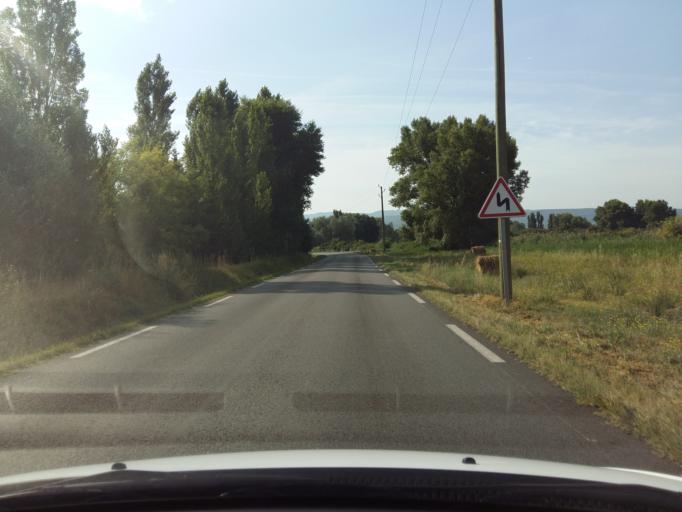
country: FR
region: Provence-Alpes-Cote d'Azur
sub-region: Departement du Vaucluse
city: Gargas
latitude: 43.9008
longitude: 5.3277
